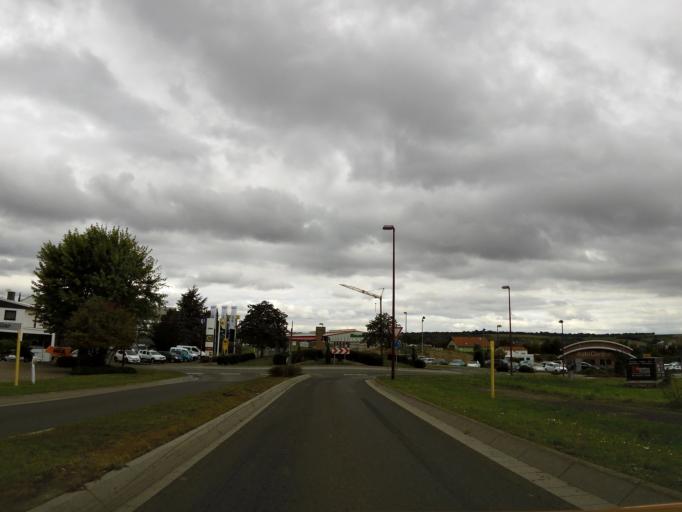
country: DE
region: Rheinland-Pfalz
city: Kirchheimbolanden
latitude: 49.6597
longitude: 8.0221
